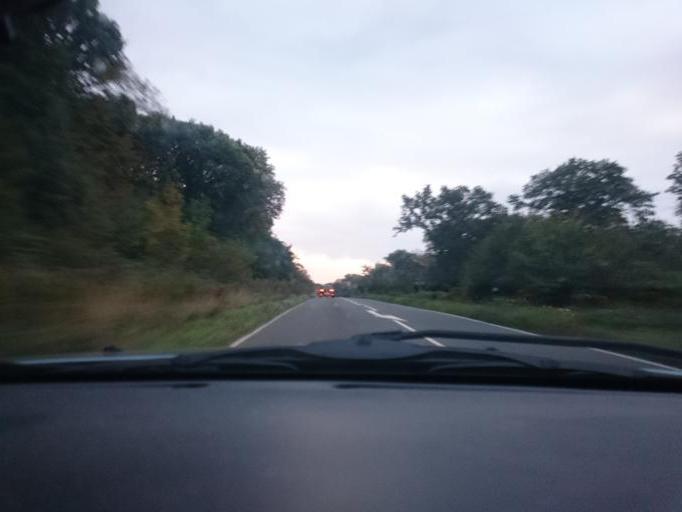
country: GB
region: England
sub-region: Hampshire
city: Kingsley
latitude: 51.1664
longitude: -0.8476
